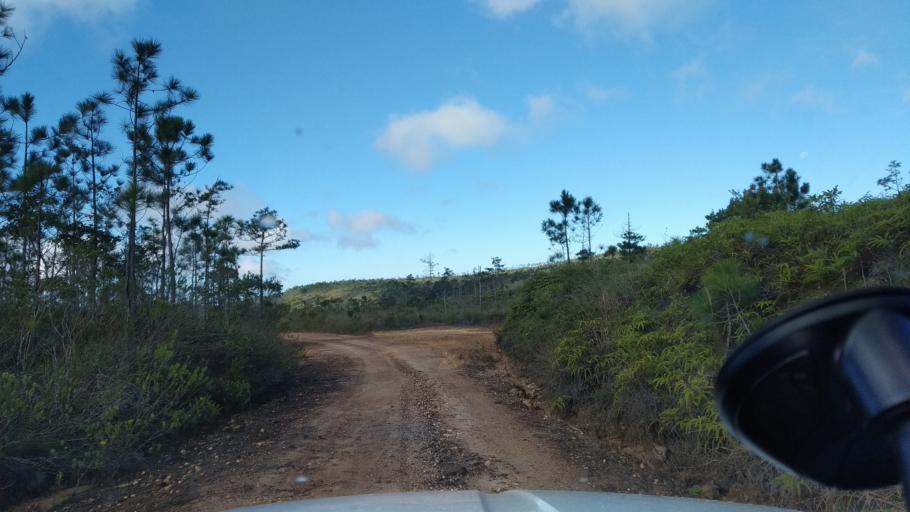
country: BZ
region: Cayo
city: Belmopan
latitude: 16.9967
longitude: -88.8339
